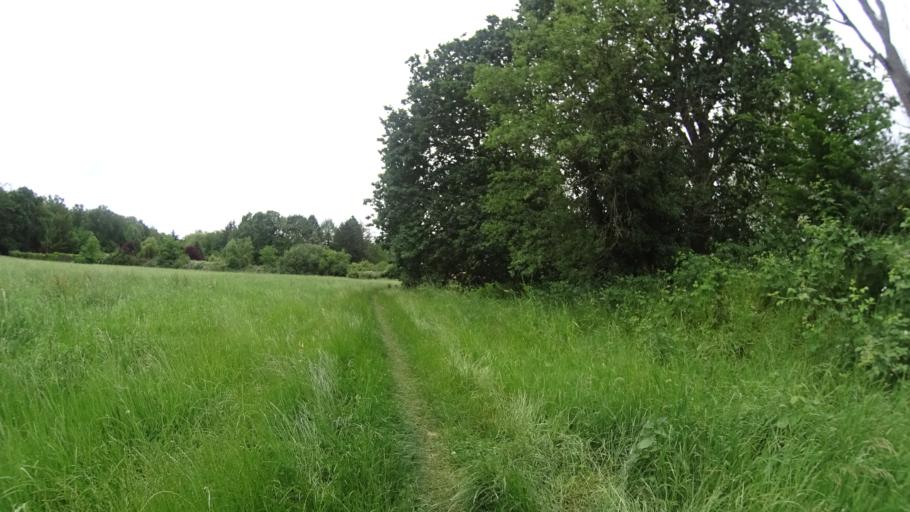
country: DE
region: Baden-Wuerttemberg
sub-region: Karlsruhe Region
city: Karlsruhe
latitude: 48.9837
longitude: 8.3839
